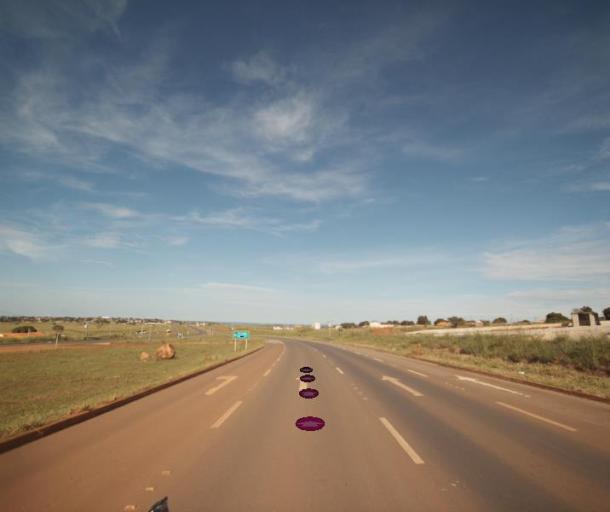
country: BR
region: Federal District
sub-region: Brasilia
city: Brasilia
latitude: -15.7414
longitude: -48.3139
